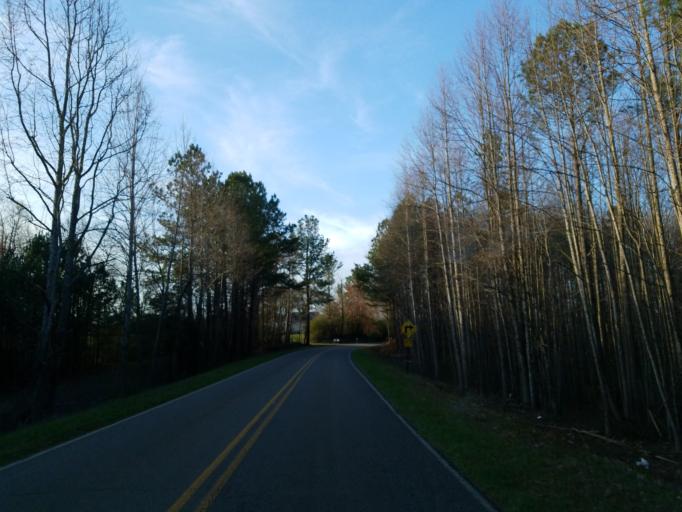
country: US
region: Georgia
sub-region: Pickens County
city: Jasper
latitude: 34.5032
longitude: -84.5222
